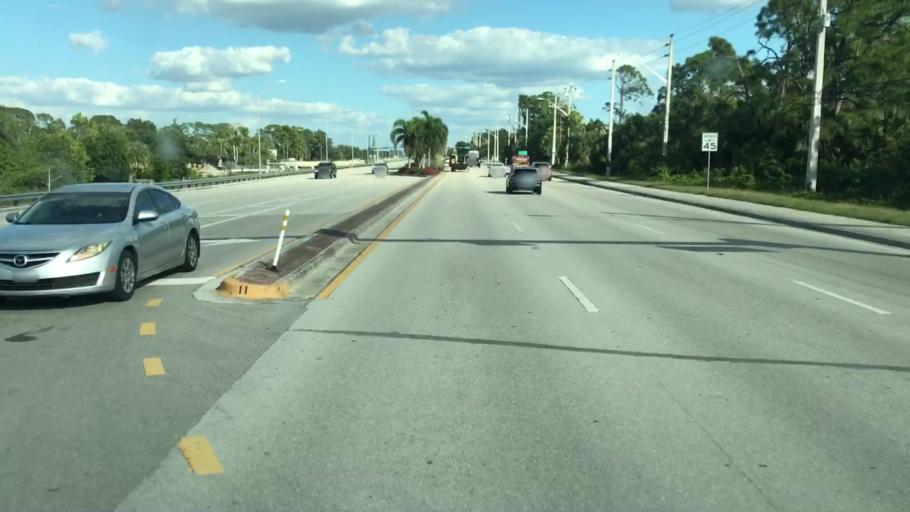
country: US
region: Florida
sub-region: Collier County
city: Naples Park
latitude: 26.2723
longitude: -81.7820
